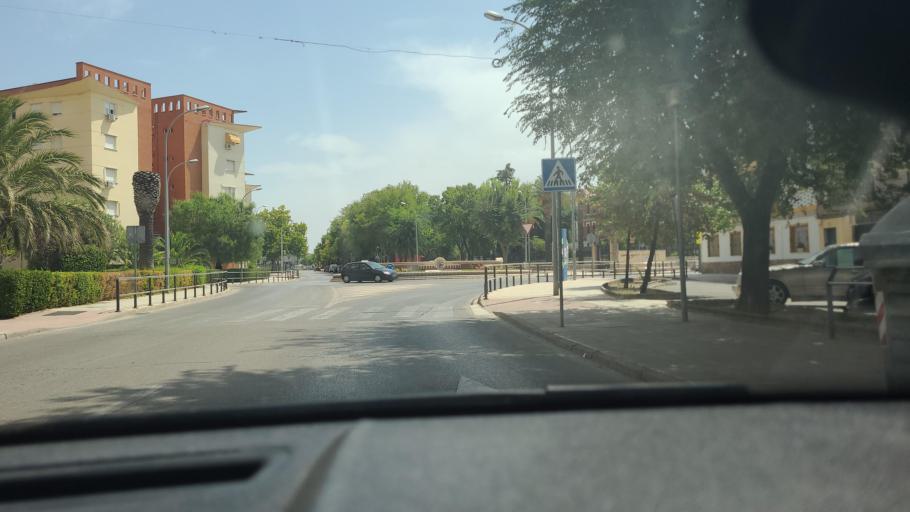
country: ES
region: Andalusia
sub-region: Provincia de Jaen
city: Linares
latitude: 38.0895
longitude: -3.6289
